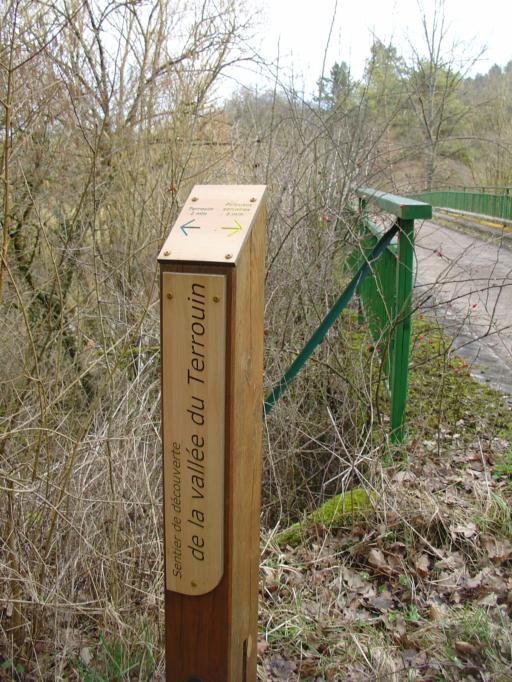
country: FR
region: Lorraine
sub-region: Departement de Meurthe-et-Moselle
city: Villey-Saint-Etienne
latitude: 48.7512
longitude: 5.9698
